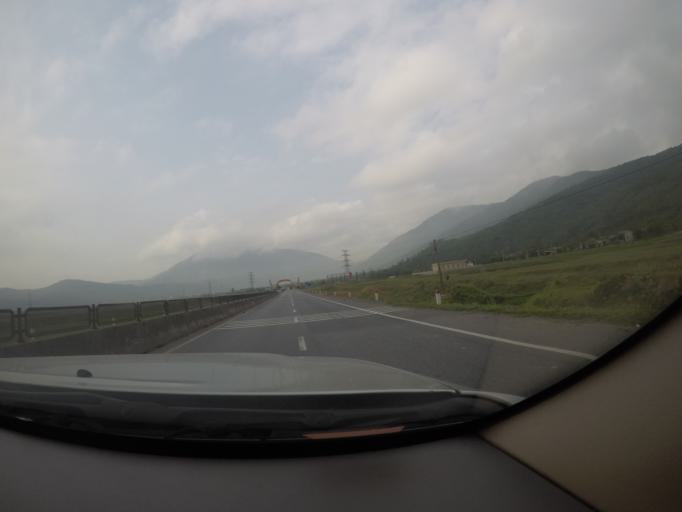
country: VN
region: Ha Tinh
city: Ky Anh
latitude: 17.9792
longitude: 106.4772
